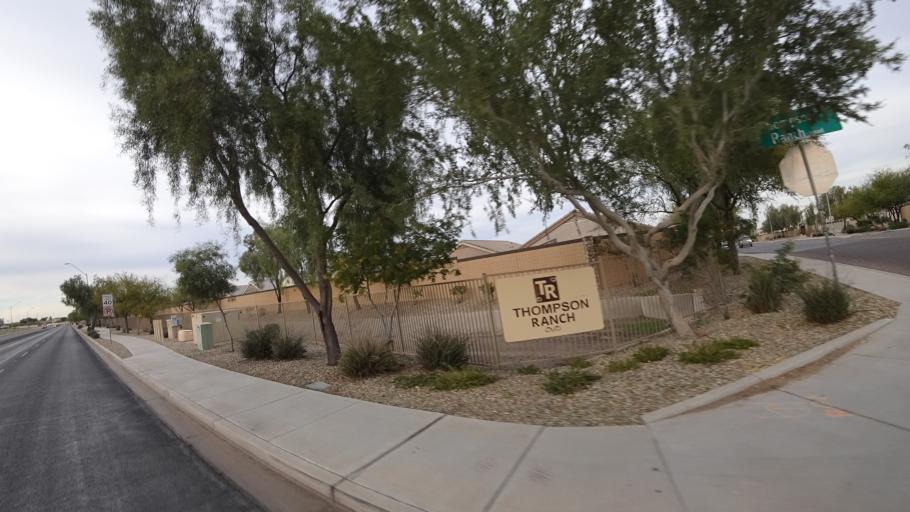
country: US
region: Arizona
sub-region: Maricopa County
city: El Mirage
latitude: 33.6203
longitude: -112.3188
